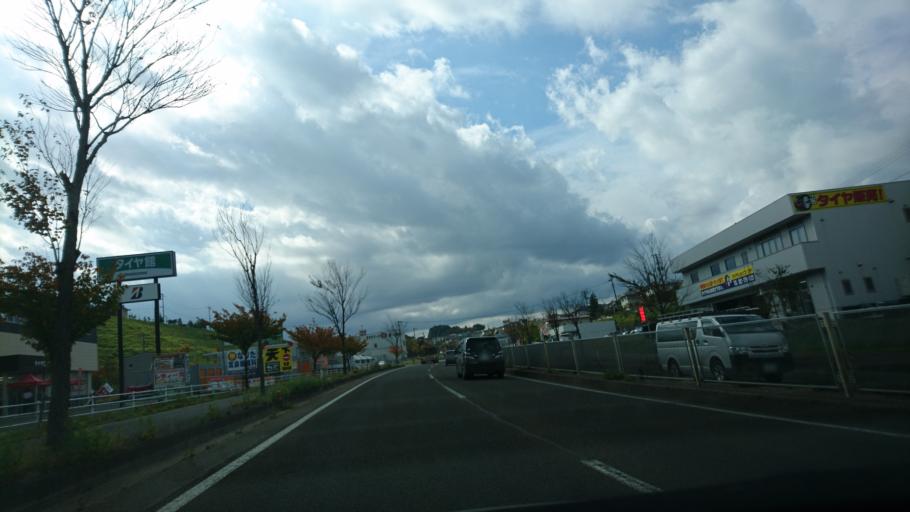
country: JP
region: Miyagi
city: Tomiya
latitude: 38.3686
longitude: 140.8741
